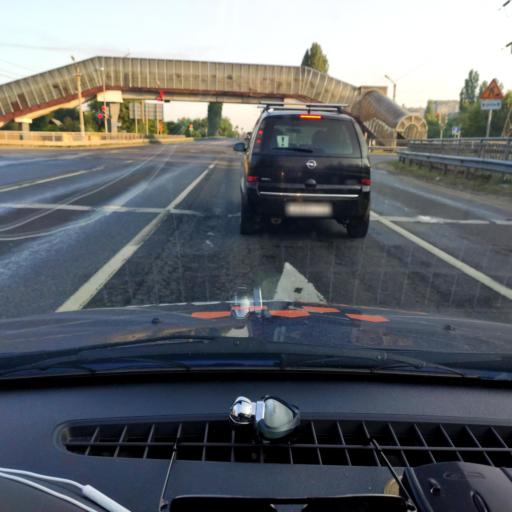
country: RU
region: Lipetsk
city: Yelets
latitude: 52.5996
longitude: 38.4738
